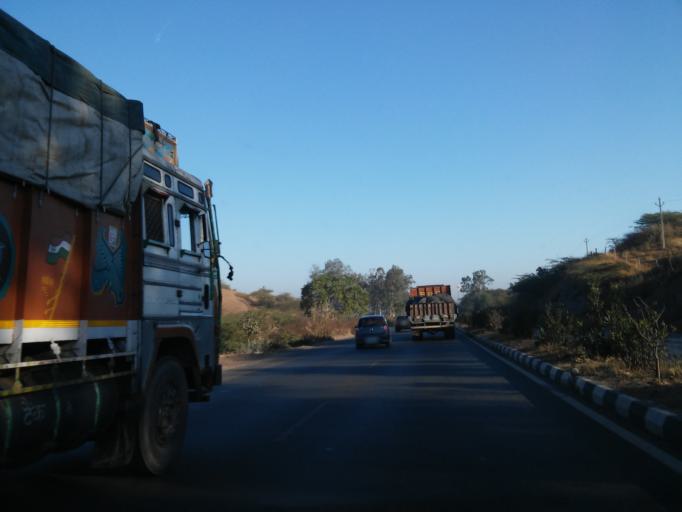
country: IN
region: Rajasthan
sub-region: Dungarpur
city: Dungarpur
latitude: 23.8496
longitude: 73.5264
